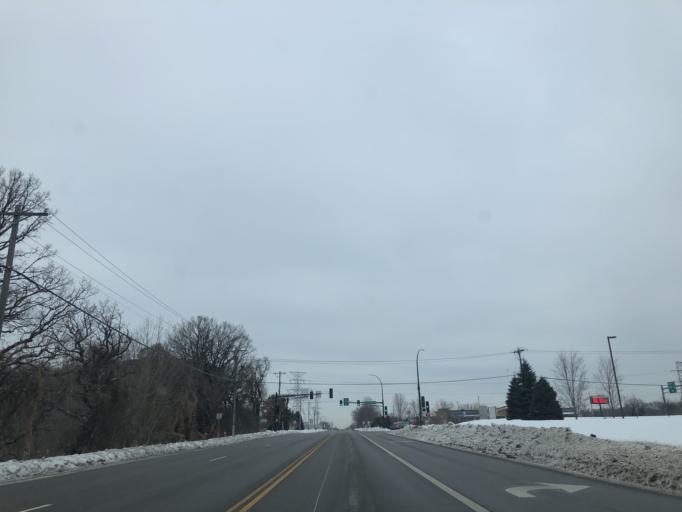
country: US
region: Minnesota
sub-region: Ramsey County
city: New Brighton
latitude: 45.0781
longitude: -93.1882
